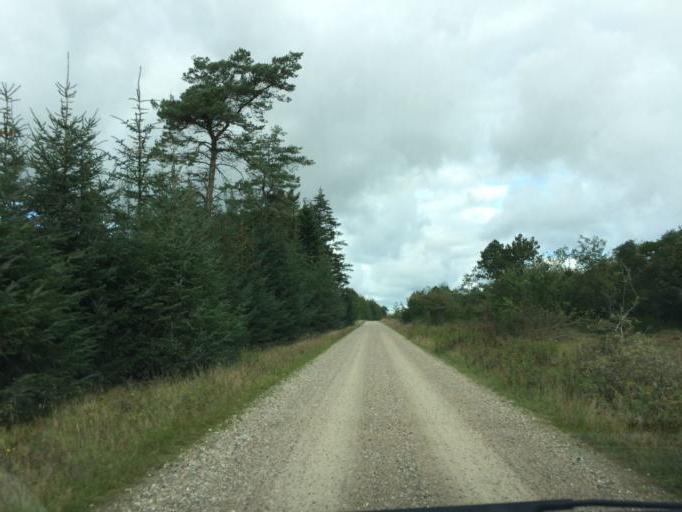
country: DK
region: Central Jutland
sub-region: Holstebro Kommune
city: Ulfborg
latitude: 56.2734
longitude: 8.4062
